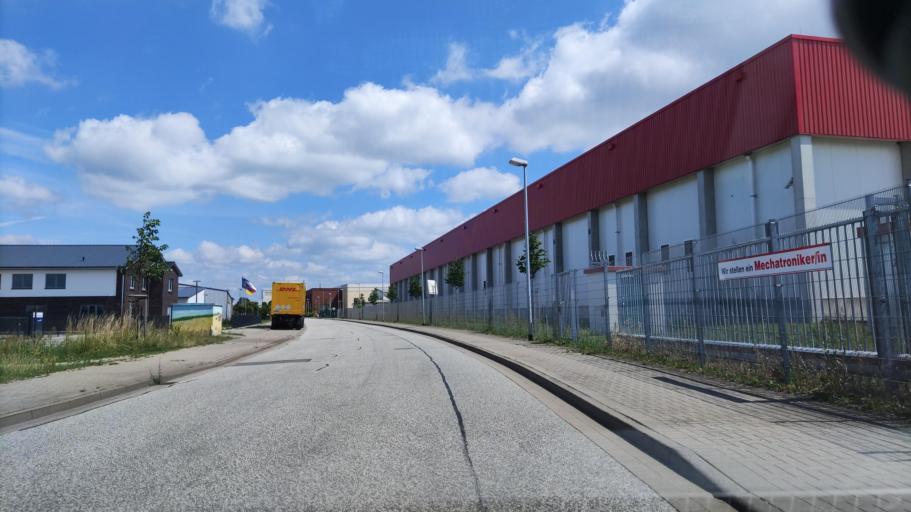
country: DE
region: Mecklenburg-Vorpommern
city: Wittenburg
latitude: 53.4999
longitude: 11.0773
